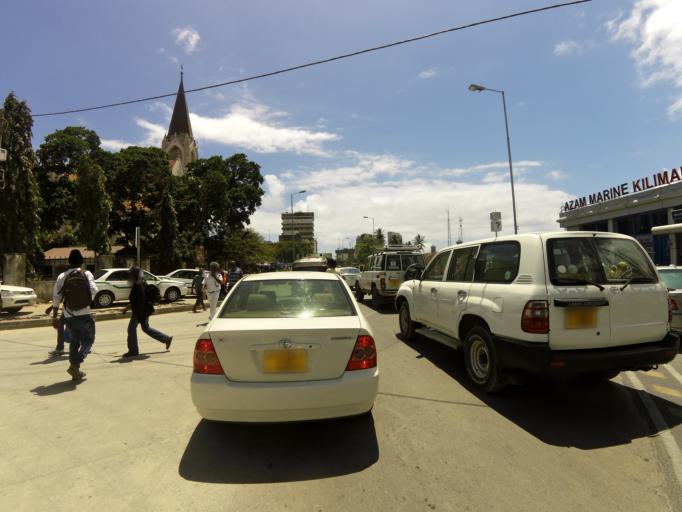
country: TZ
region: Dar es Salaam
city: Dar es Salaam
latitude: -6.8201
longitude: 39.2877
